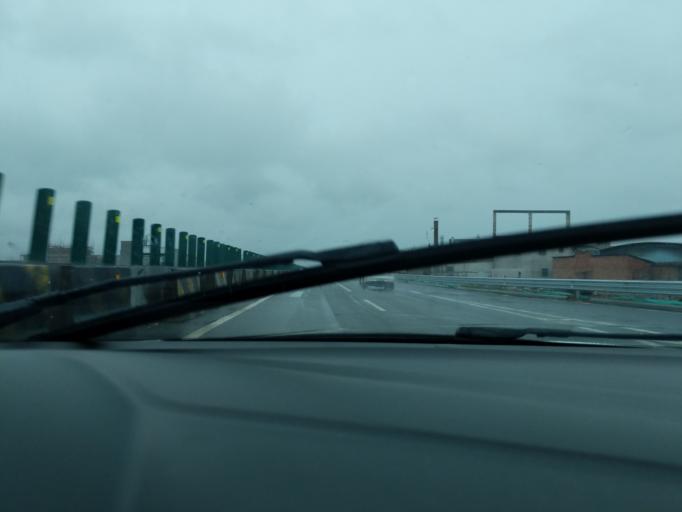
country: CN
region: Guangdong
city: Shuikou
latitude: 22.4728
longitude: 112.7630
